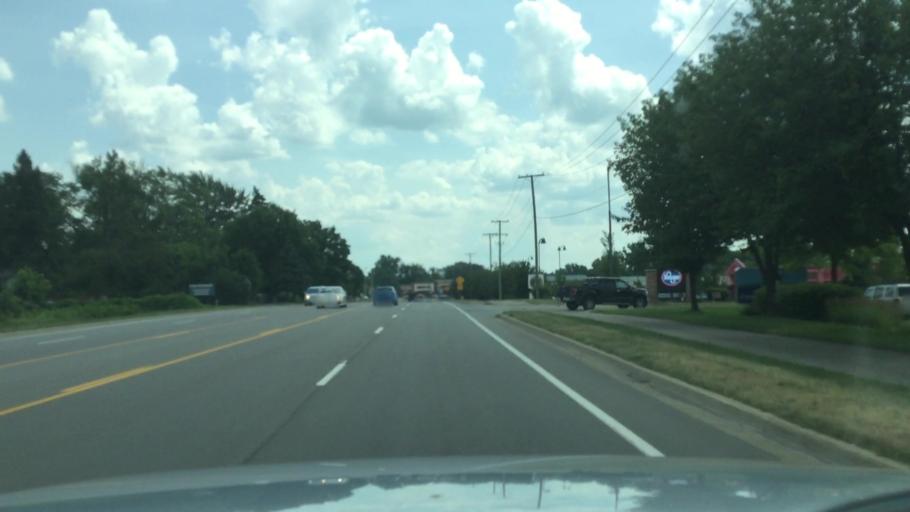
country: US
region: Michigan
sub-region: Washtenaw County
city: Ypsilanti
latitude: 42.2136
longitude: -83.6194
